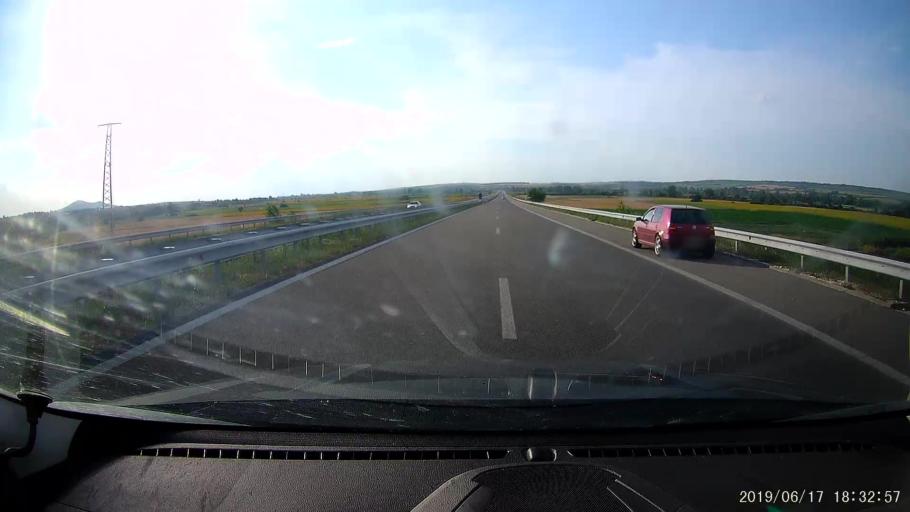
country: BG
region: Khaskovo
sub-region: Obshtina Dimitrovgrad
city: Dimitrovgrad
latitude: 42.0693
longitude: 25.4677
